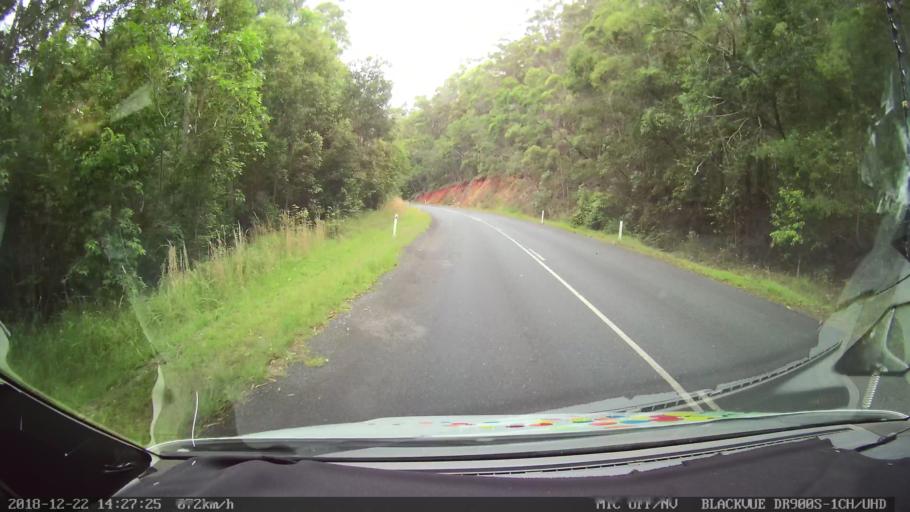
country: AU
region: New South Wales
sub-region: Bellingen
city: Dorrigo
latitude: -30.0653
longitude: 152.6347
